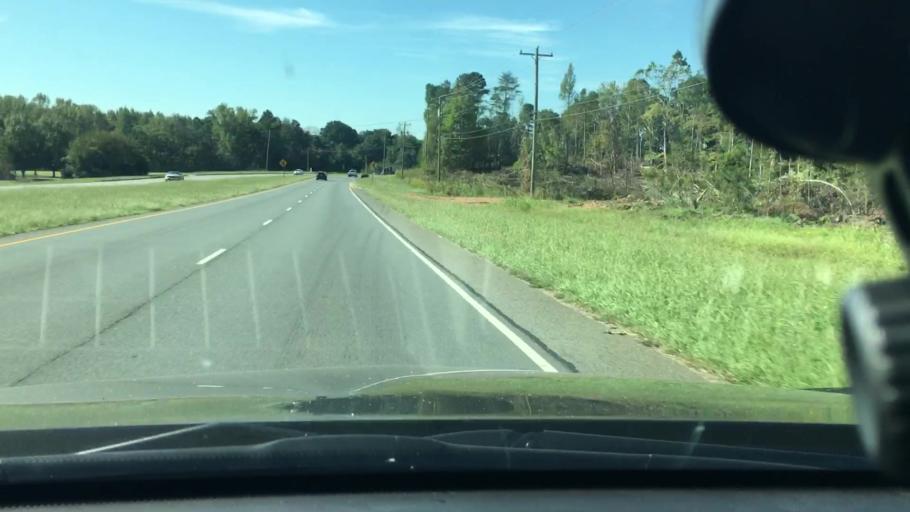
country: US
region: North Carolina
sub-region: Mecklenburg County
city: Mint Hill
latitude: 35.2372
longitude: -80.5974
